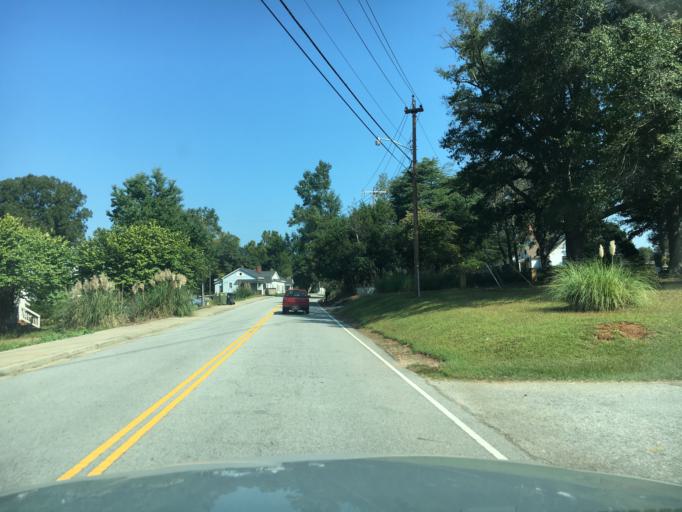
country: US
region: South Carolina
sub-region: Spartanburg County
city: Wellford
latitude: 34.9341
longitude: -82.0958
